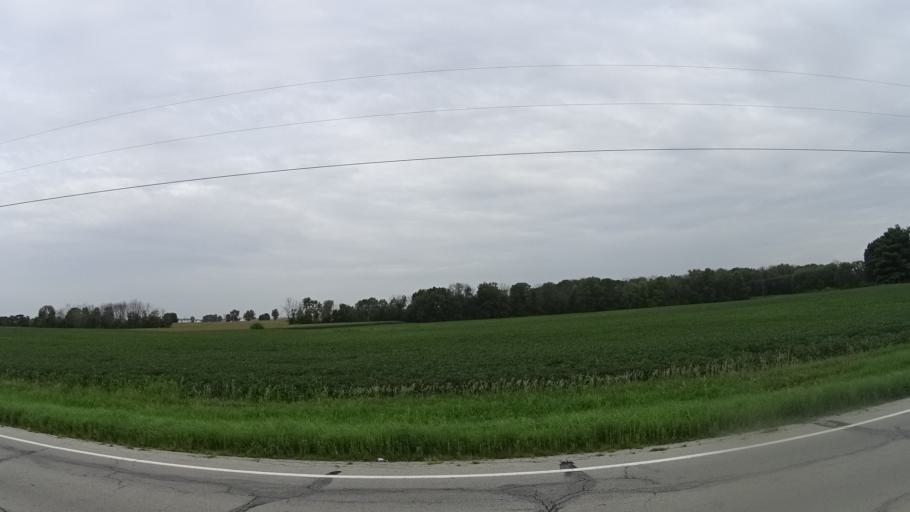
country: US
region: Indiana
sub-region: Madison County
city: Lapel
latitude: 40.0829
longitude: -85.8317
